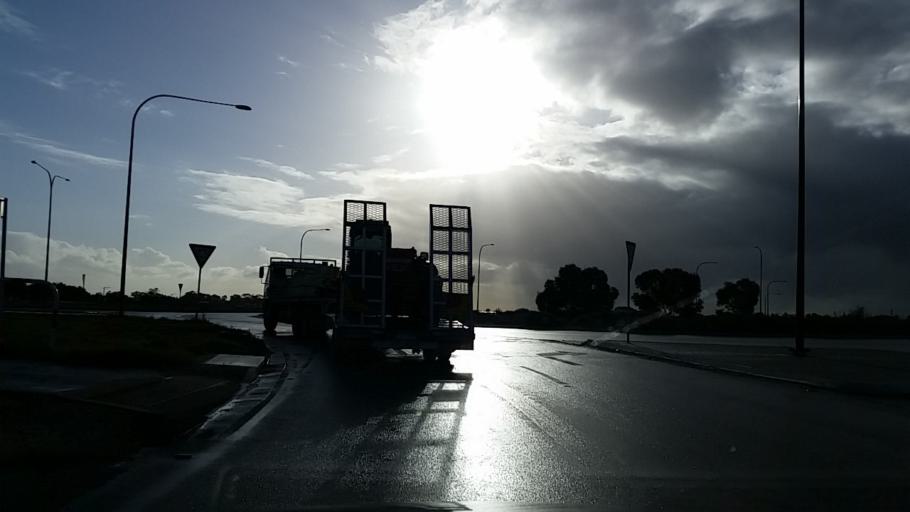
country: AU
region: South Australia
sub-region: Playford
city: Angle Vale
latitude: -34.6820
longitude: 138.6224
